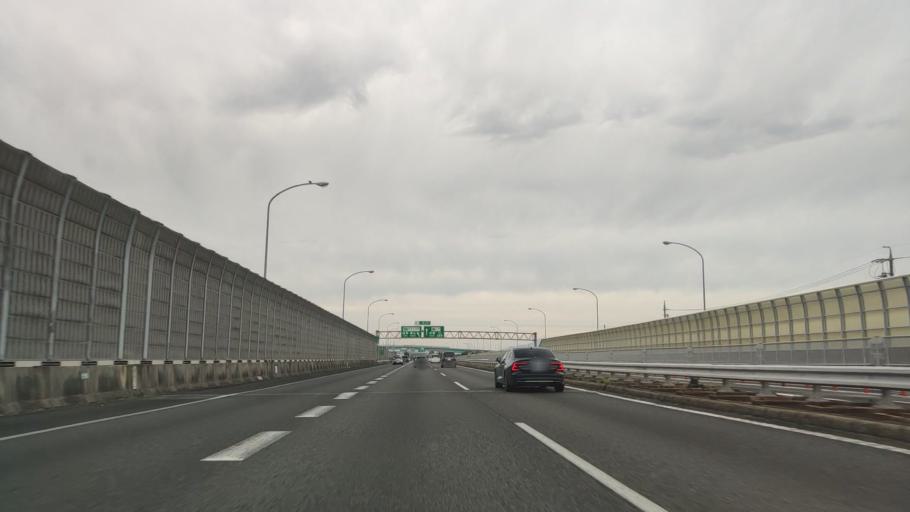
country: JP
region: Aichi
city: Ichinomiya
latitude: 35.2808
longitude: 136.7909
